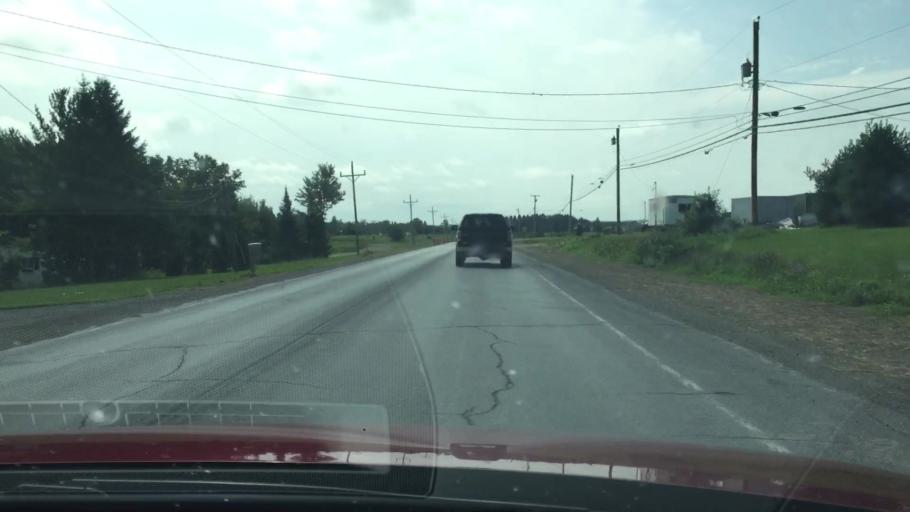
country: US
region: Maine
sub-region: Aroostook County
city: Easton
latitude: 46.4977
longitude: -67.8685
